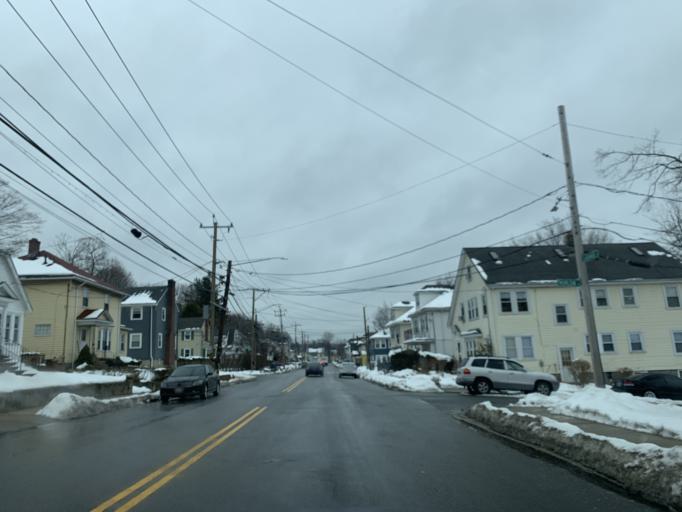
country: US
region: Massachusetts
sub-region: Norfolk County
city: Dedham
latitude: 42.2858
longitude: -71.1638
